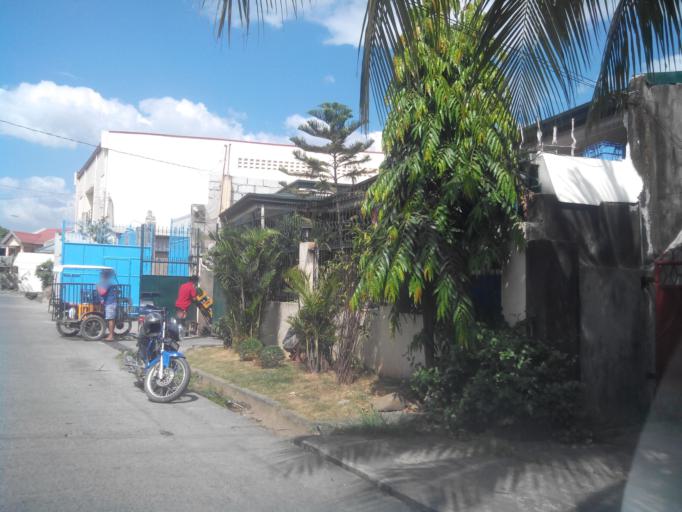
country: PH
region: Calabarzon
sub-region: Province of Rizal
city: Taytay
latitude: 14.5565
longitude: 121.1391
